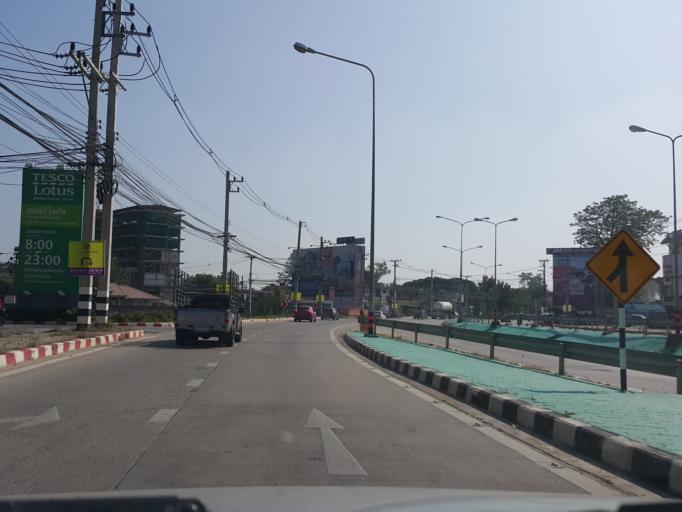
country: TH
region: Chiang Mai
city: San Sai
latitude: 18.8231
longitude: 99.0139
